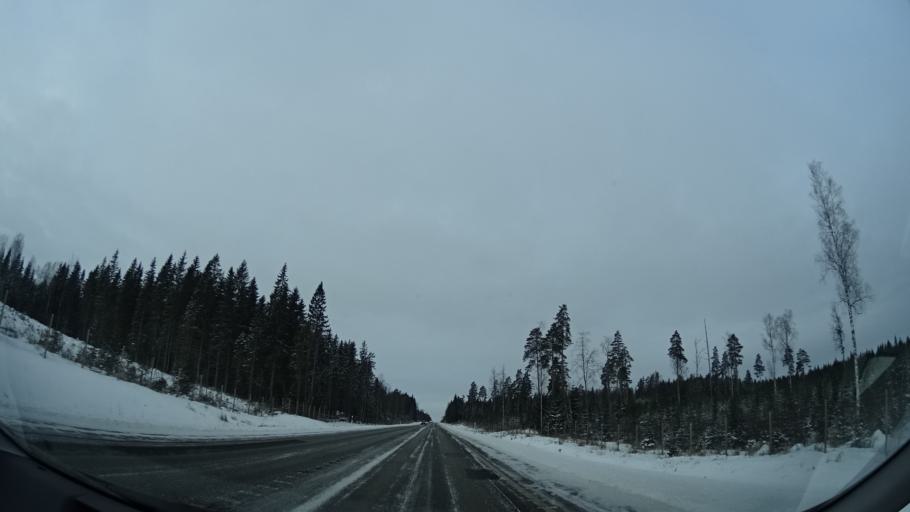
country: FI
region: Uusimaa
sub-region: Helsinki
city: Kaerkoelae
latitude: 60.6247
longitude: 23.9720
